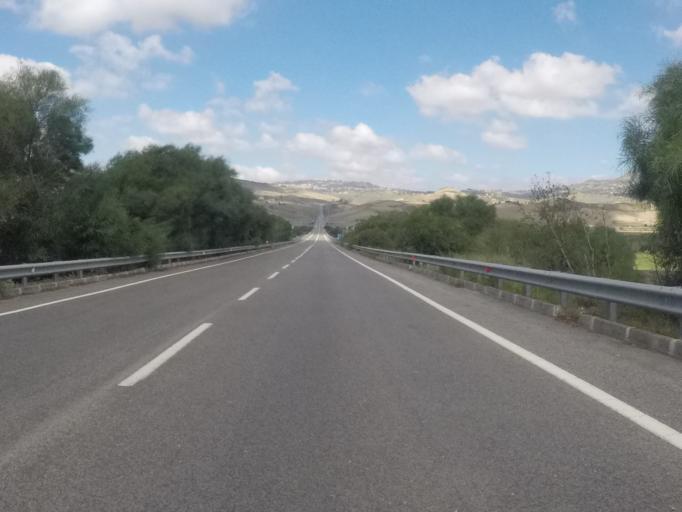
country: IT
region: Sicily
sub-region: Enna
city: Pietraperzia
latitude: 37.4493
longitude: 14.1153
